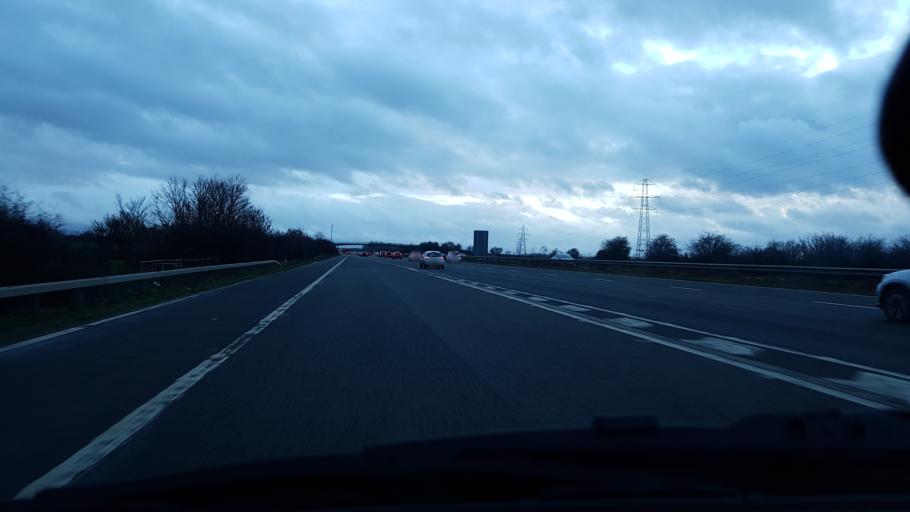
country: GB
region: England
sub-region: Gloucestershire
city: Tewkesbury
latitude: 51.9932
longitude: -2.1238
